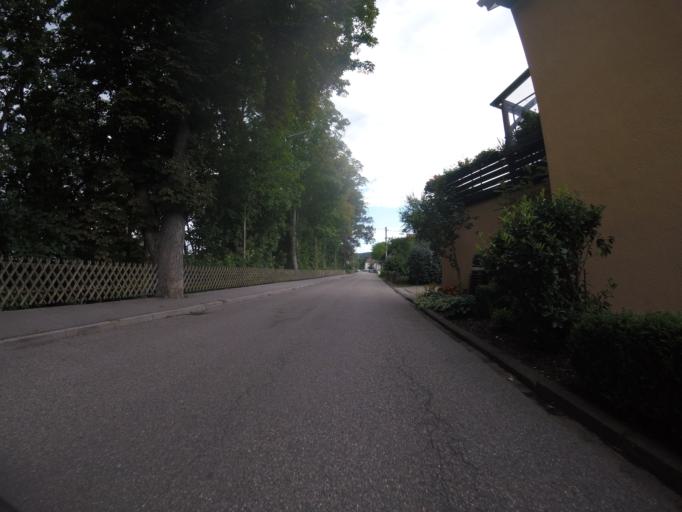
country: DE
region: Baden-Wuerttemberg
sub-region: Regierungsbezirk Stuttgart
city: Lorch
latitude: 48.7965
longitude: 9.6882
